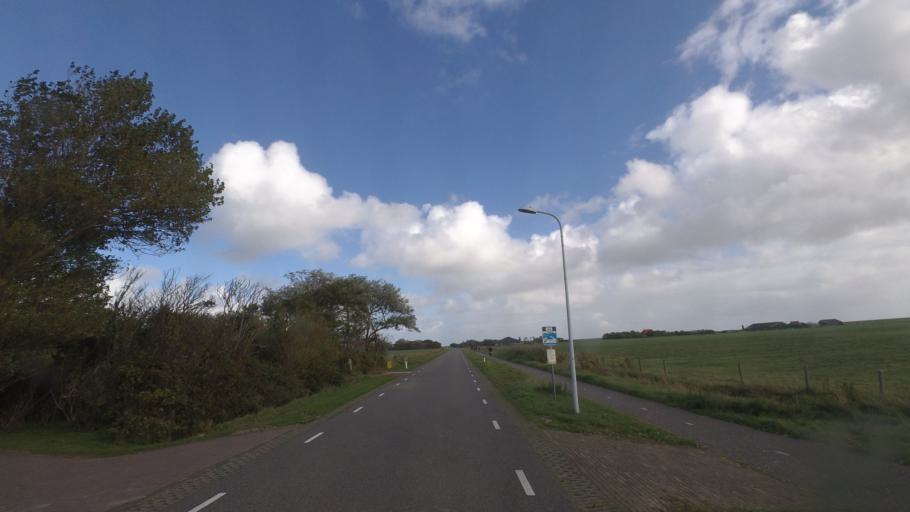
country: NL
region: Friesland
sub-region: Gemeente Ameland
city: Hollum
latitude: 53.4373
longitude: 5.6558
